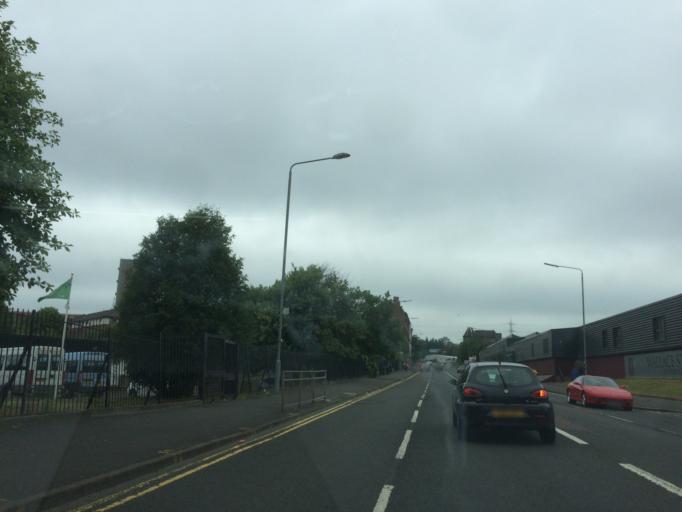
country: GB
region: Scotland
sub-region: Glasgow City
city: Glasgow
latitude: 55.8712
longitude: -4.2606
